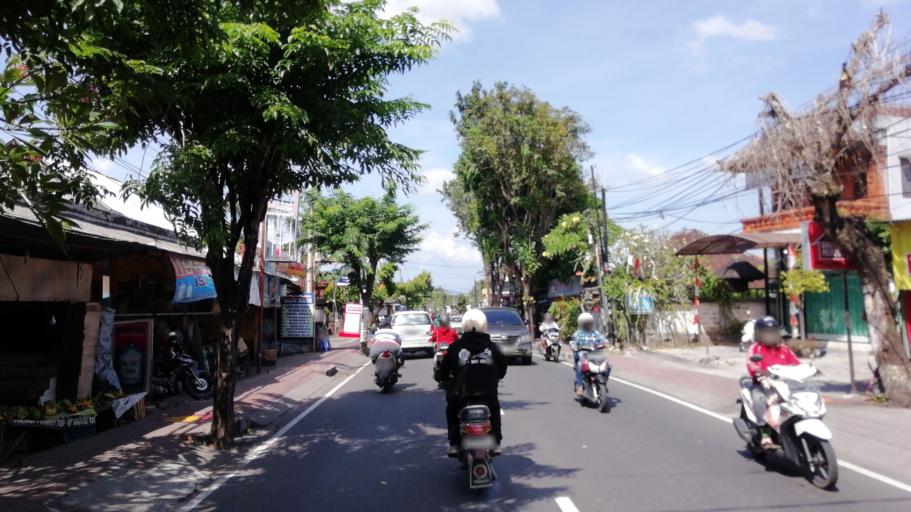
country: ID
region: Bali
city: Banjar Gunungpande
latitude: -8.6455
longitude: 115.1685
